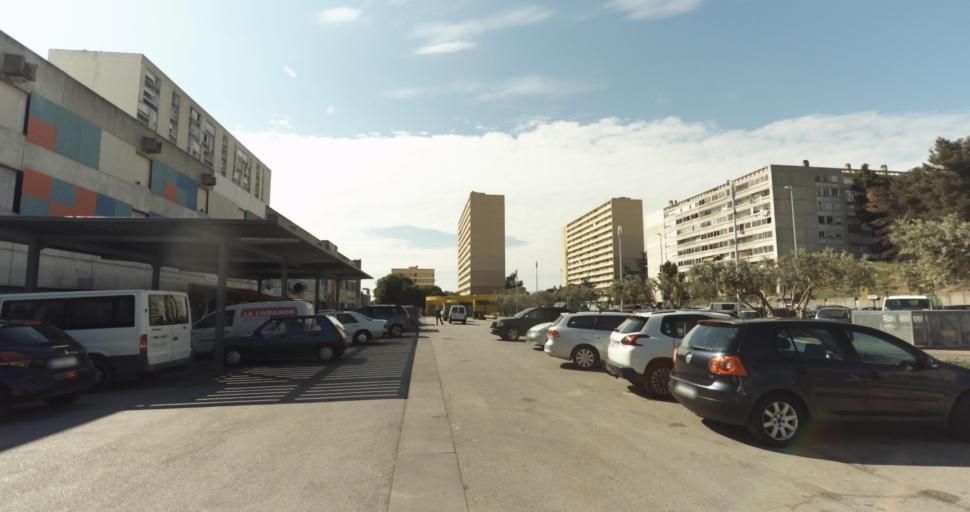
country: FR
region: Languedoc-Roussillon
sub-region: Departement du Gard
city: Nimes
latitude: 43.8243
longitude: 4.3358
